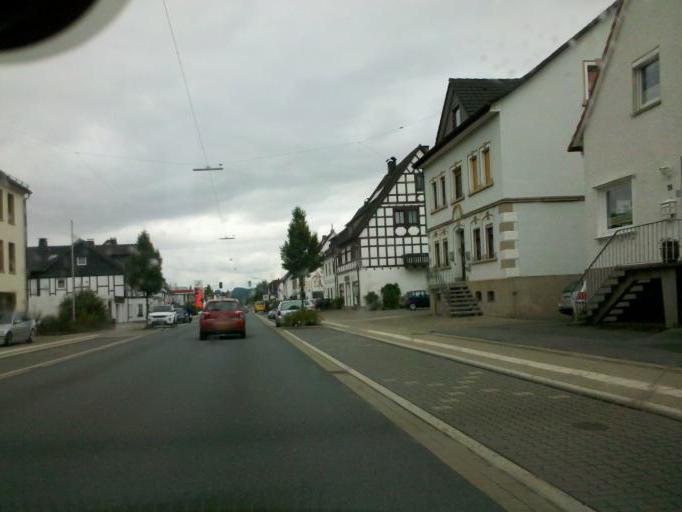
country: DE
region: North Rhine-Westphalia
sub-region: Regierungsbezirk Arnsberg
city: Lennestadt
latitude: 51.1540
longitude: 8.0514
